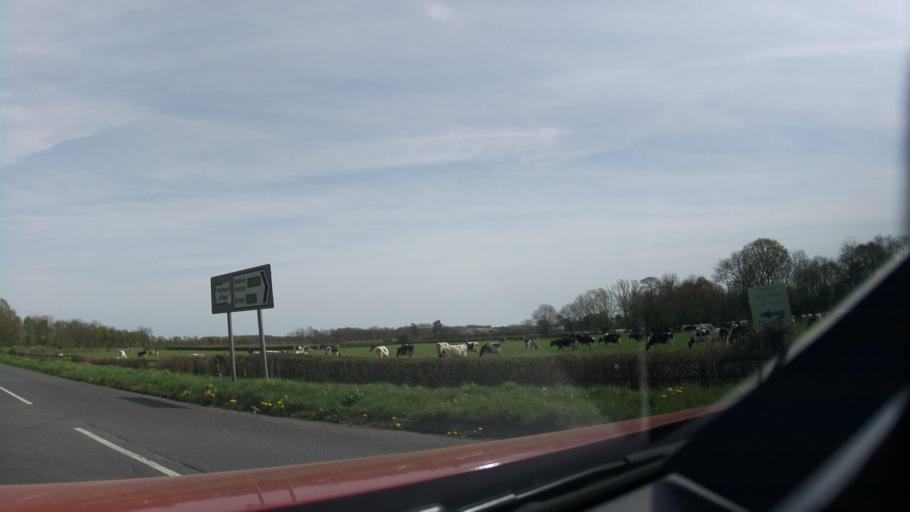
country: GB
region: England
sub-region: Somerset
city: Ilchester
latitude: 51.0222
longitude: -2.6602
